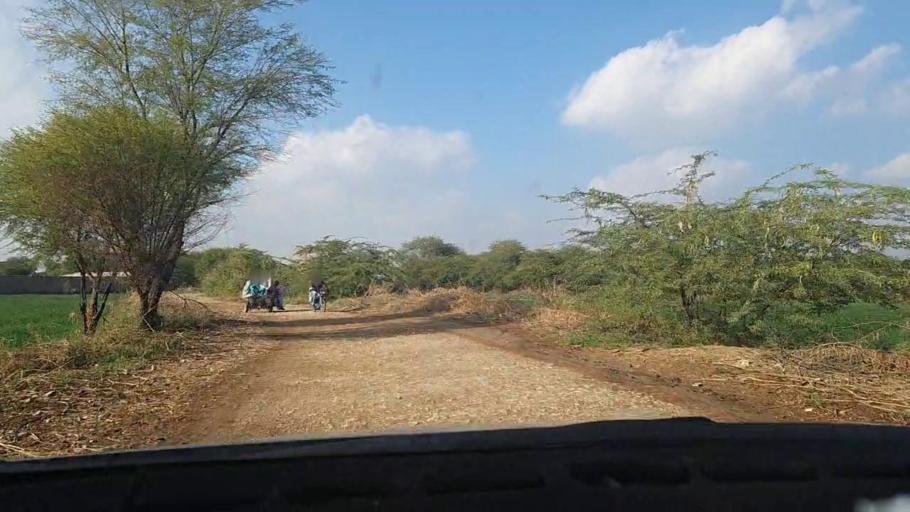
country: PK
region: Sindh
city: Tando Mittha Khan
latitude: 25.8761
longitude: 69.2927
